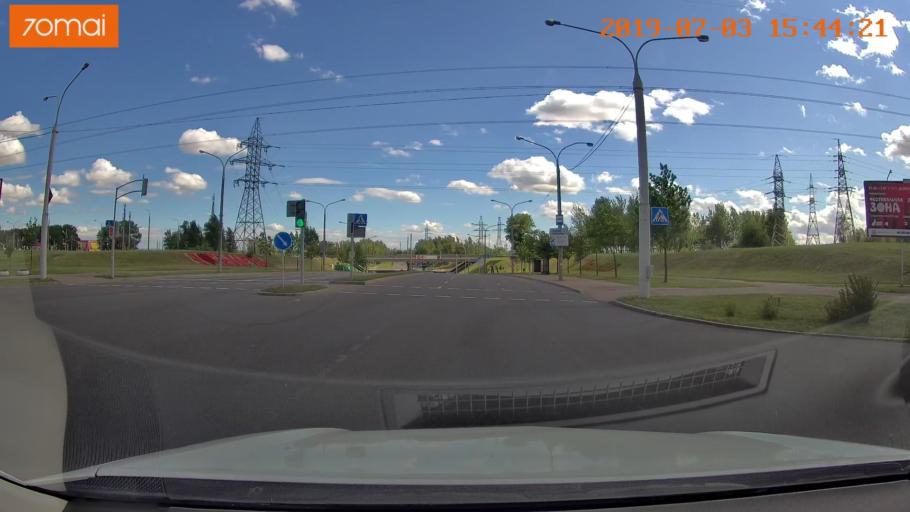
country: BY
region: Minsk
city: Syenitsa
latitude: 53.8355
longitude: 27.5744
